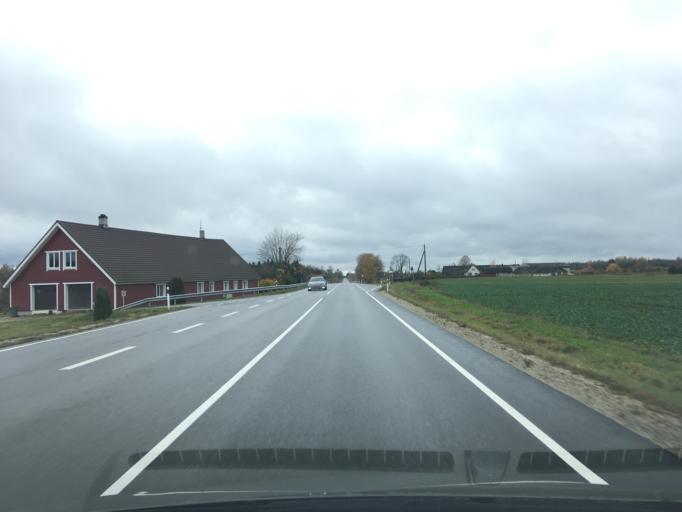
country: EE
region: Jogevamaa
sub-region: Tabivere vald
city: Tabivere
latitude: 58.4574
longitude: 26.5335
